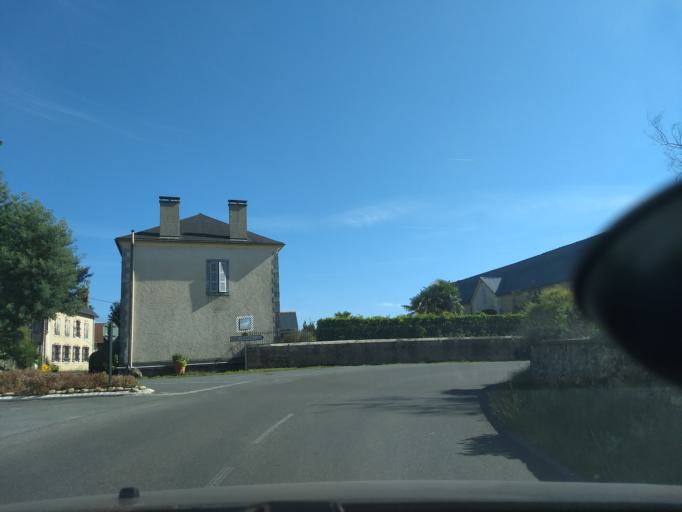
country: FR
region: Aquitaine
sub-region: Departement des Pyrenees-Atlantiques
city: Soumoulou
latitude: 43.2748
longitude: -0.1823
